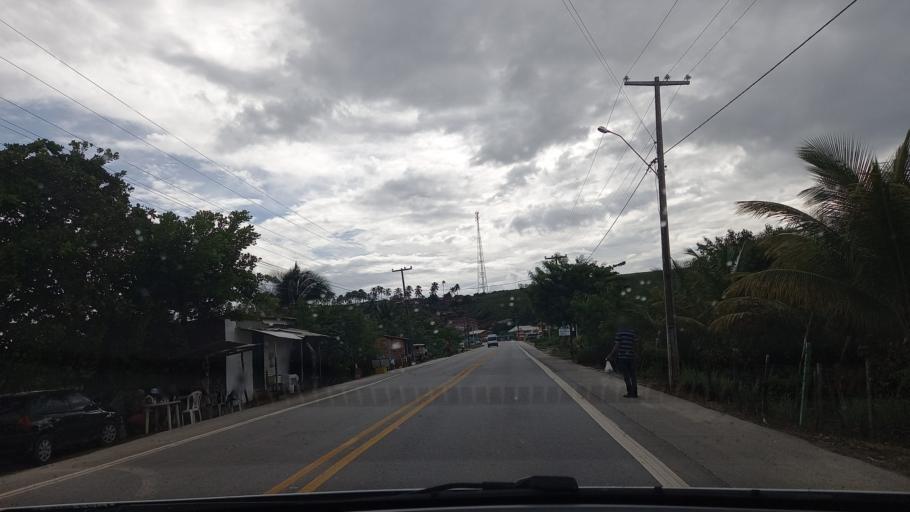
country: BR
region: Alagoas
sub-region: Maragogi
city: Maragogi
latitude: -8.9820
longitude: -35.1919
